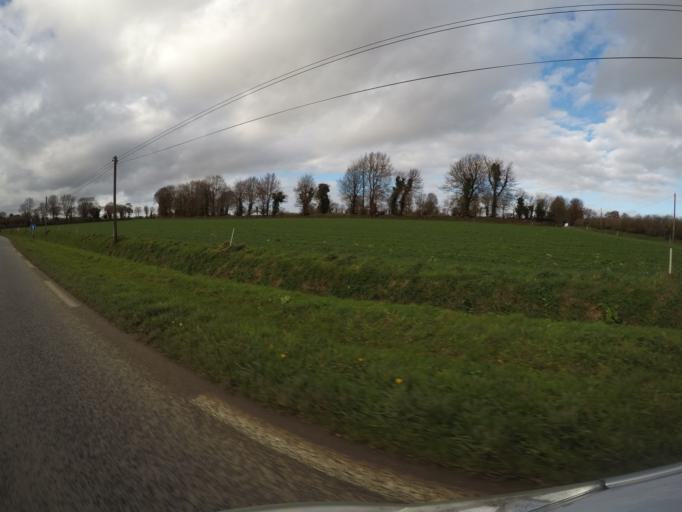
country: FR
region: Brittany
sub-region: Departement des Cotes-d'Armor
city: Callac
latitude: 48.4514
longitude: -3.3597
